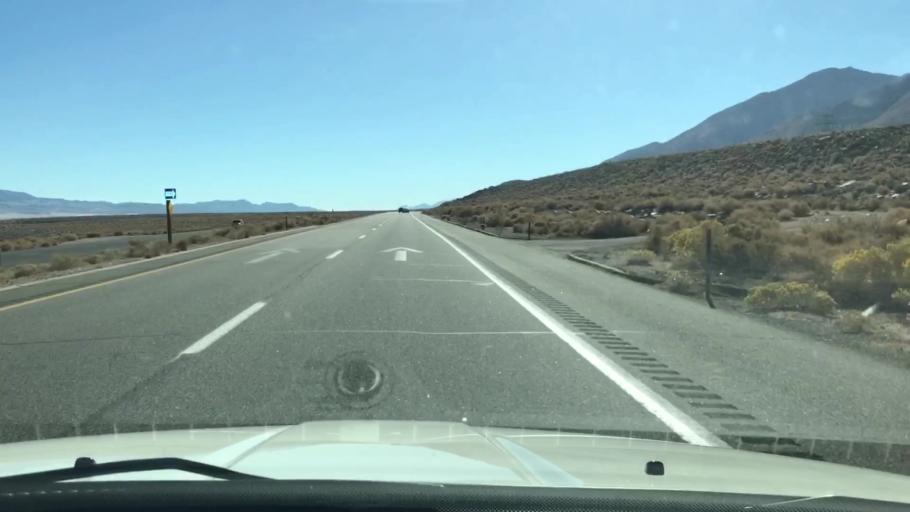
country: US
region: California
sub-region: Inyo County
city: Lone Pine
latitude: 36.4555
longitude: -118.0353
